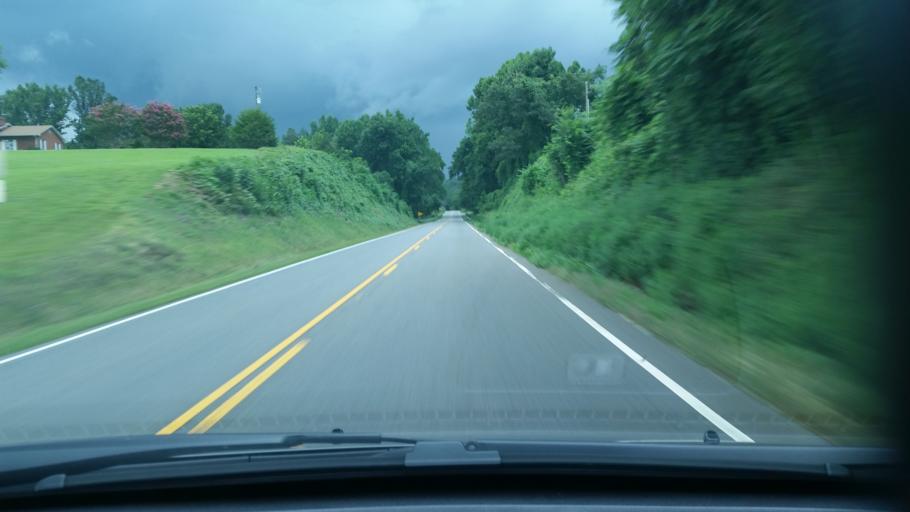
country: US
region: Virginia
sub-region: Nelson County
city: Nellysford
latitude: 37.8817
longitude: -78.8221
